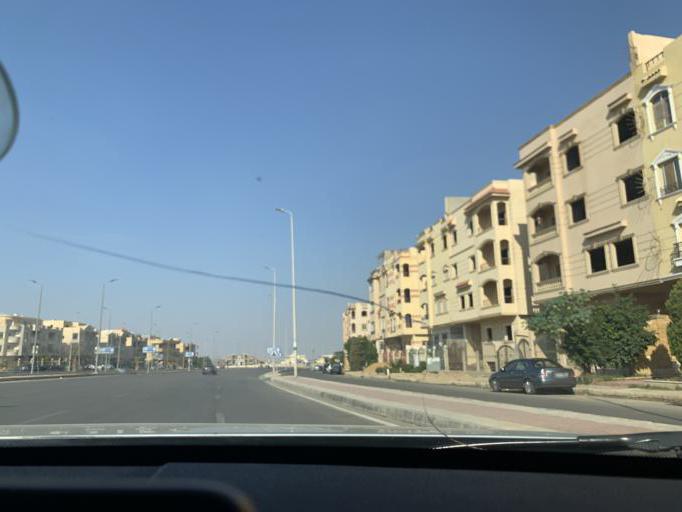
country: EG
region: Muhafazat al Qahirah
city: Cairo
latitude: 30.0039
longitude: 31.4690
